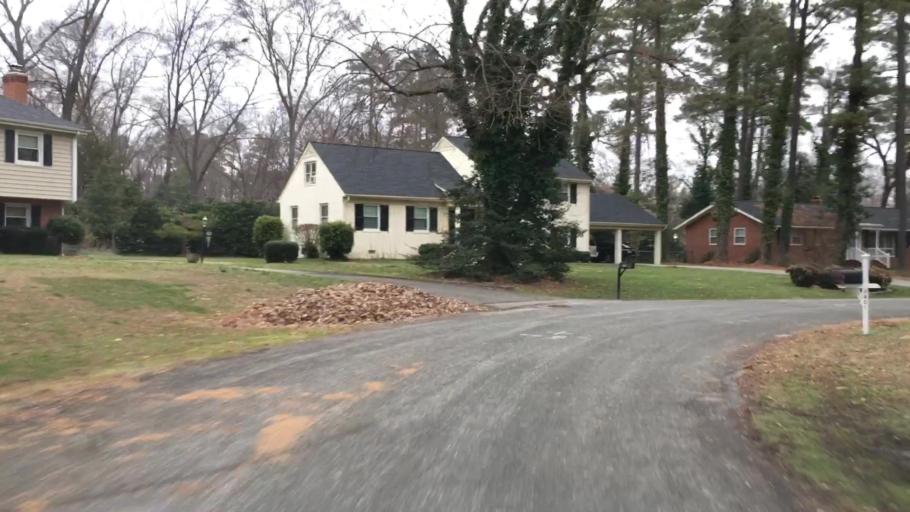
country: US
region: Virginia
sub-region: Chesterfield County
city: Bon Air
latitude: 37.5343
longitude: -77.5794
